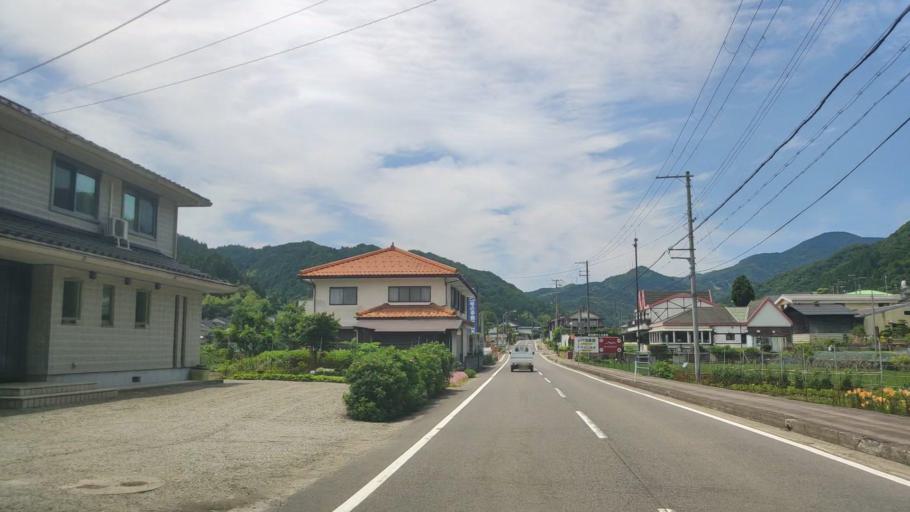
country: JP
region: Hyogo
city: Toyooka
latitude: 35.4691
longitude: 134.5491
